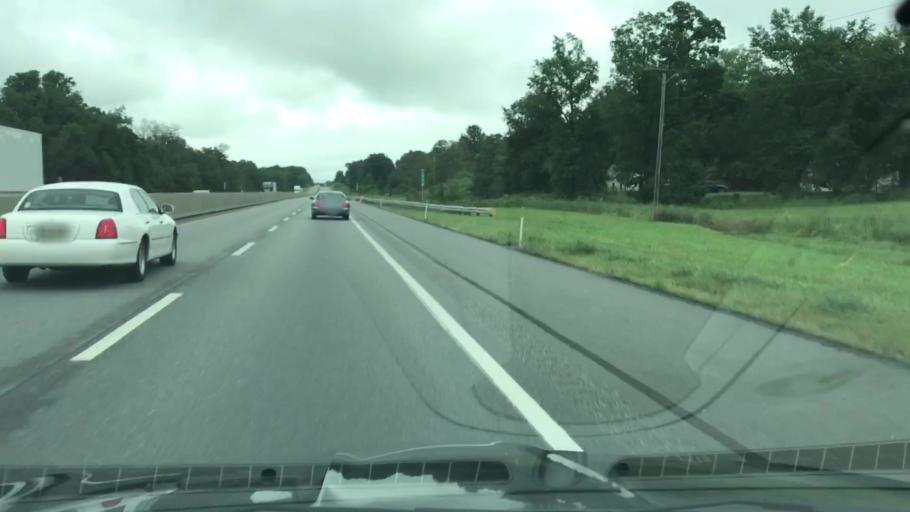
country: US
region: Pennsylvania
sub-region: Franklin County
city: Doylestown
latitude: 40.1438
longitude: -77.7248
